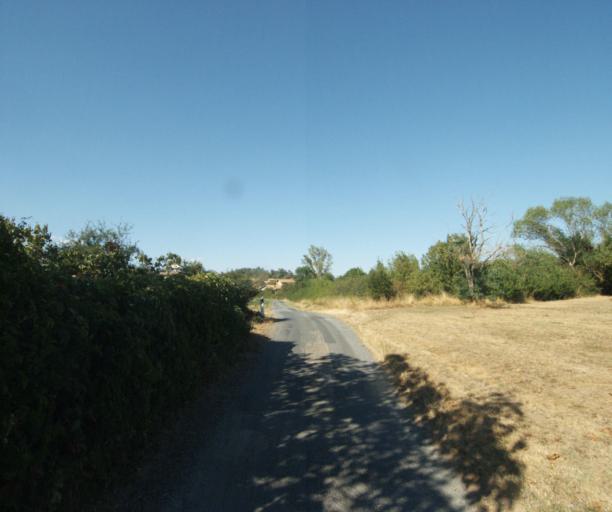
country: FR
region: Rhone-Alpes
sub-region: Departement du Rhone
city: Lentilly
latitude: 45.8190
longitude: 4.6770
